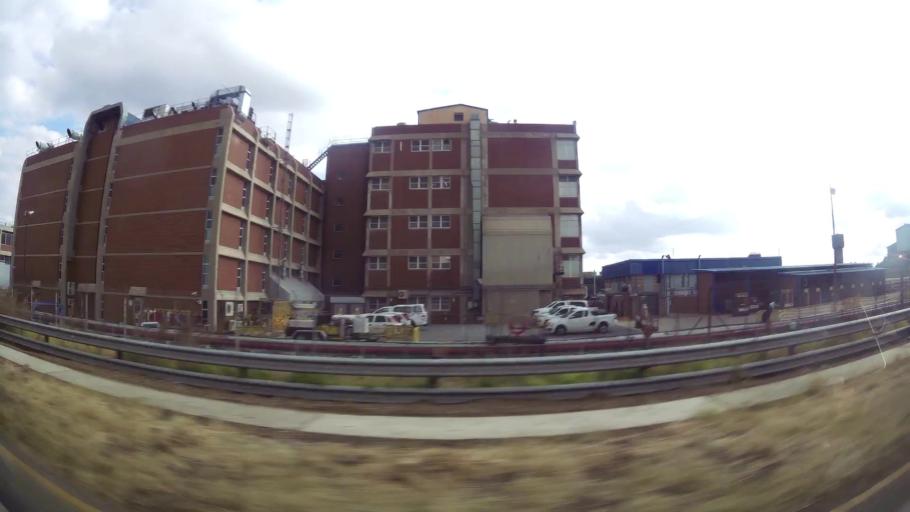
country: ZA
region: Orange Free State
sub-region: Fezile Dabi District Municipality
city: Sasolburg
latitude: -26.8198
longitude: 27.8441
